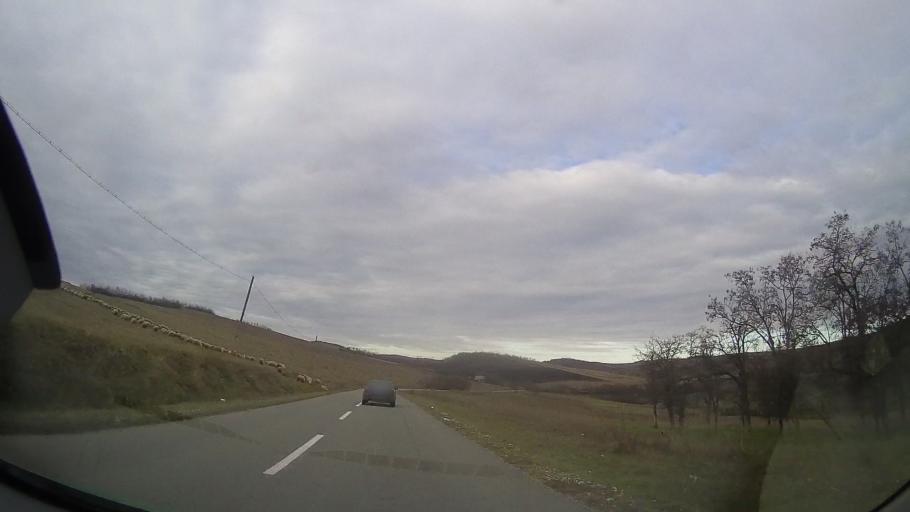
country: RO
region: Bistrita-Nasaud
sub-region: Comuna Milas
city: Milas
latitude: 46.8273
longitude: 24.4507
